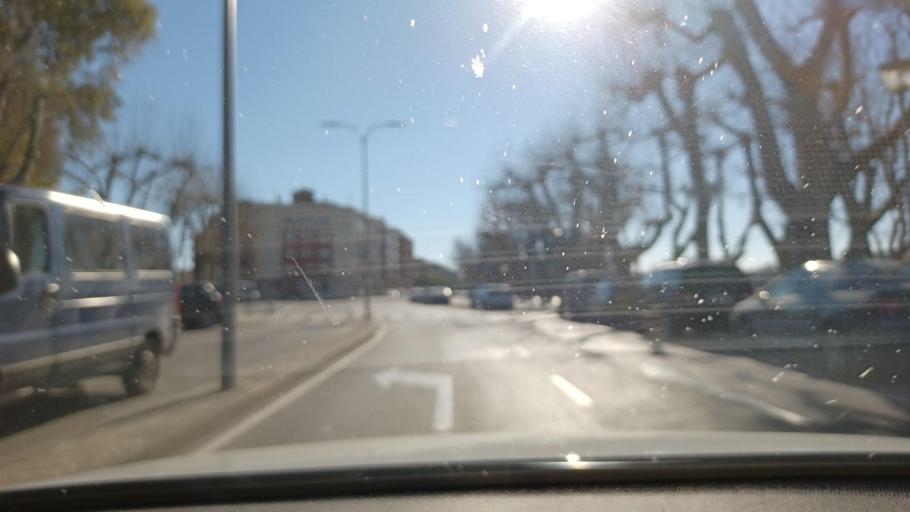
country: ES
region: Catalonia
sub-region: Provincia de Tarragona
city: Tortosa
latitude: 40.8086
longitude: 0.5178
